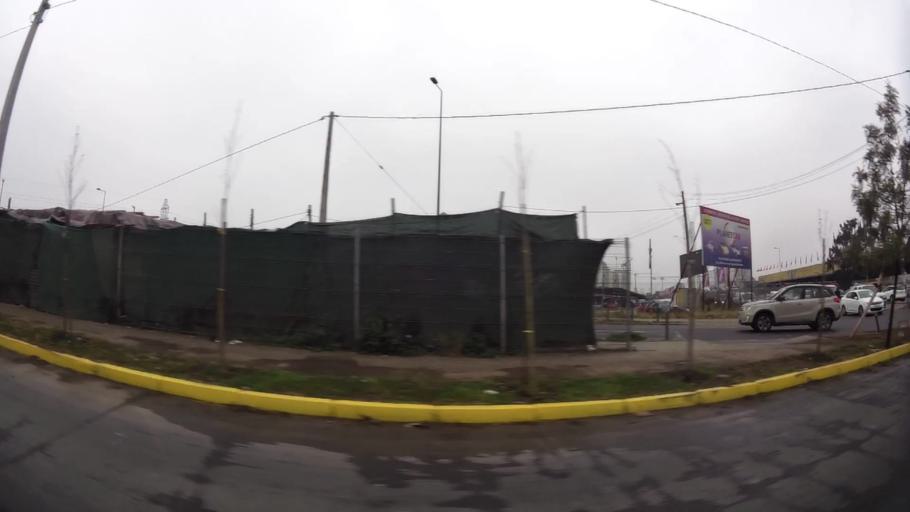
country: CL
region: Santiago Metropolitan
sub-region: Provincia de Santiago
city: Santiago
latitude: -33.4766
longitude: -70.6436
